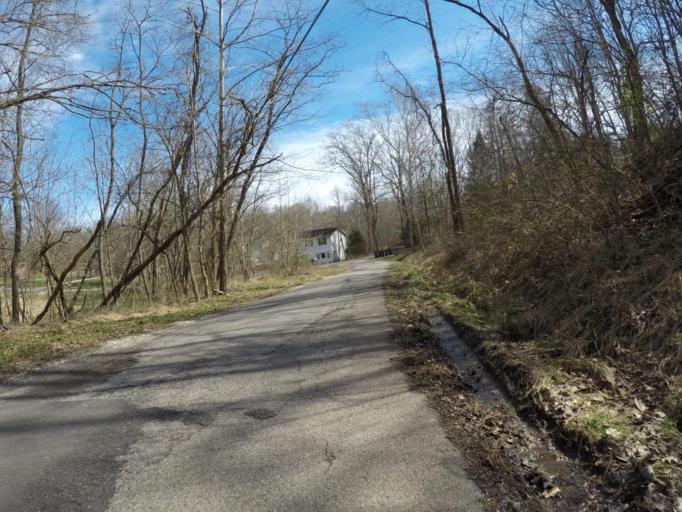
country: US
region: West Virginia
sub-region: Wayne County
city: Ceredo
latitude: 38.3623
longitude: -82.5321
